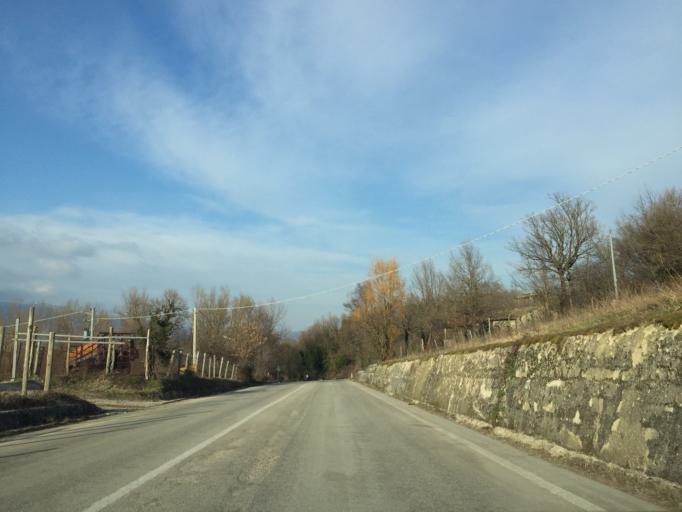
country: IT
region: Molise
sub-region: Provincia di Campobasso
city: San Massimo
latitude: 41.4872
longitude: 14.4052
